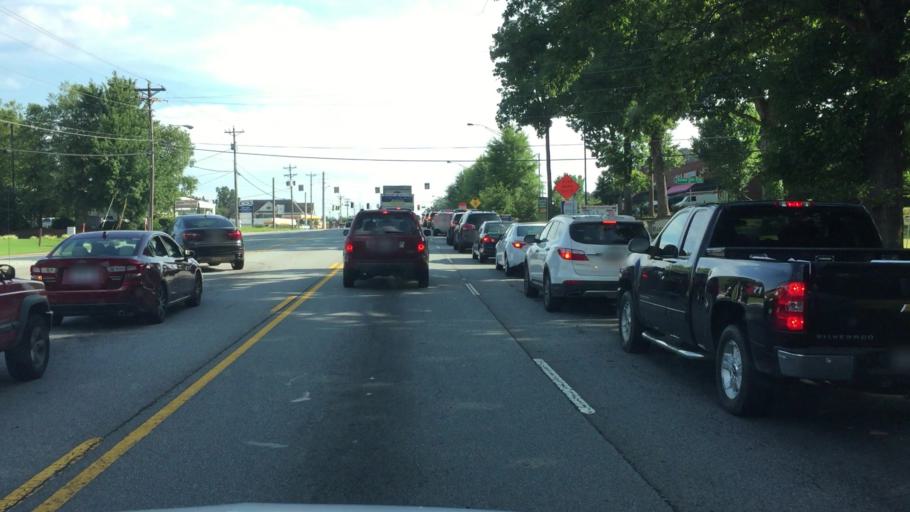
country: US
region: Georgia
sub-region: Gwinnett County
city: Snellville
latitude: 33.8623
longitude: -84.0181
